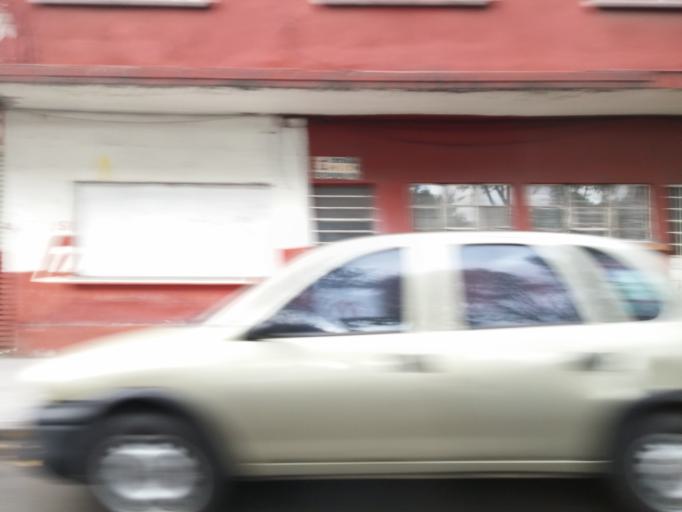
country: MX
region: Mexico City
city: Azcapotzalco
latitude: 19.4617
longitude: -99.1756
